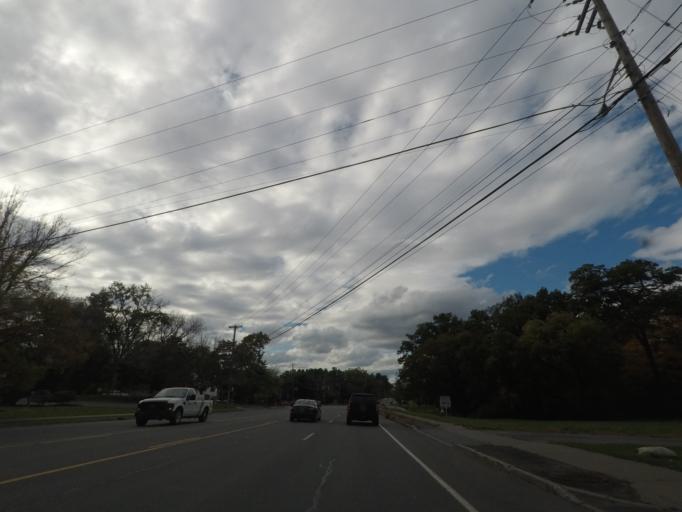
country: US
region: New York
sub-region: Albany County
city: Westmere
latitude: 42.6930
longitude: -73.8752
